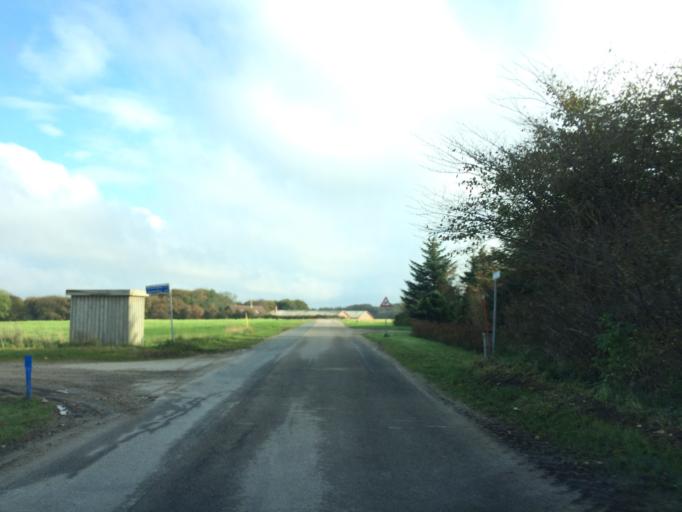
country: DK
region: Central Jutland
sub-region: Holstebro Kommune
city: Holstebro
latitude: 56.3539
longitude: 8.5432
